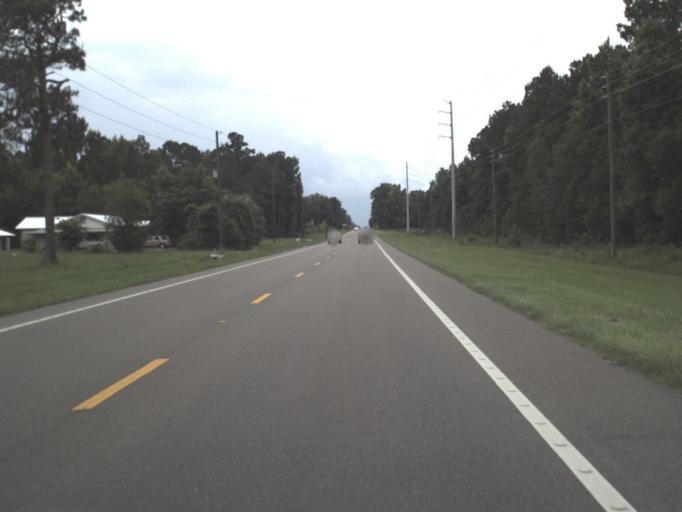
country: US
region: Florida
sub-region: Clay County
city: Keystone Heights
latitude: 29.8486
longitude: -82.0687
